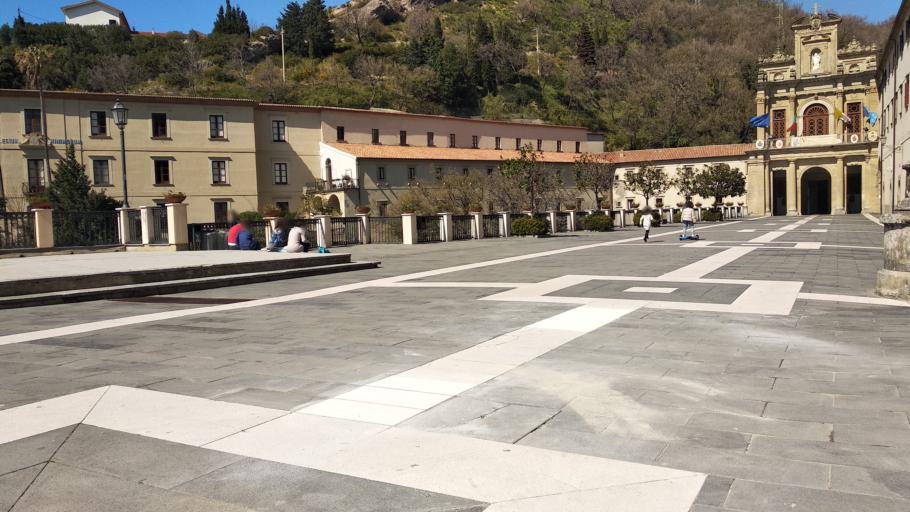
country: IT
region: Calabria
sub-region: Provincia di Cosenza
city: Paola
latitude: 39.3685
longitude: 16.0452
